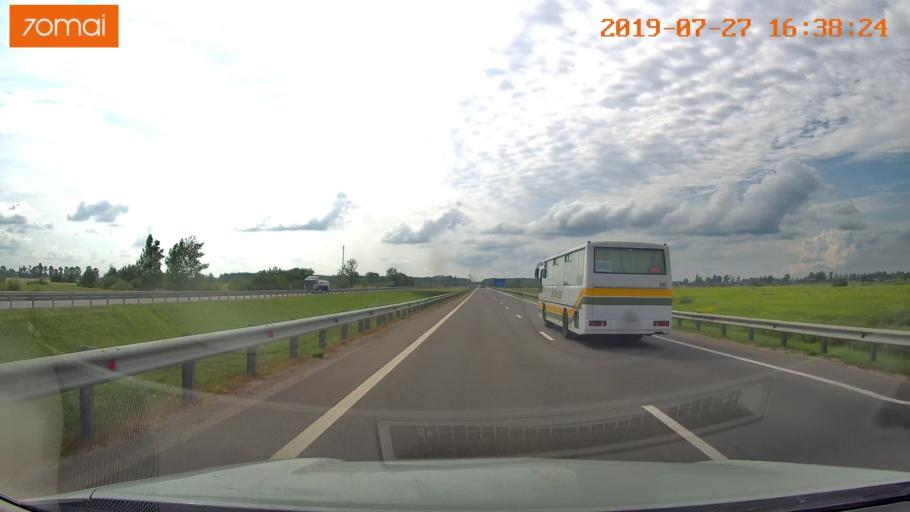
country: RU
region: Kaliningrad
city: Gvardeysk
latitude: 54.6488
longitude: 21.2291
